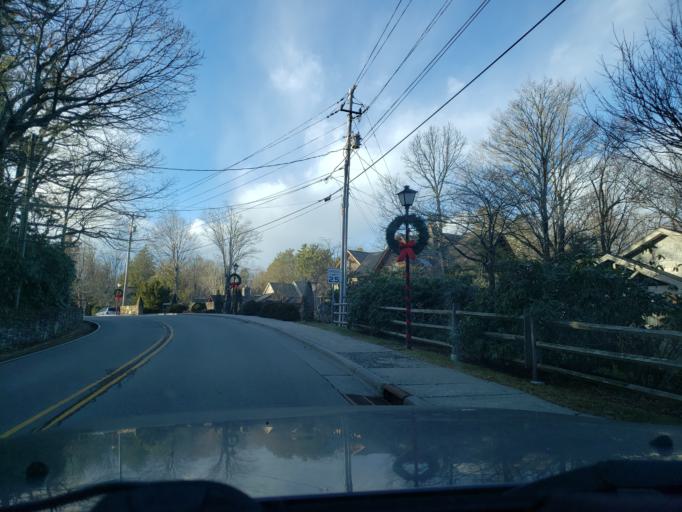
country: US
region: North Carolina
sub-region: Watauga County
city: Blowing Rock
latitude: 36.1239
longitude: -81.6759
